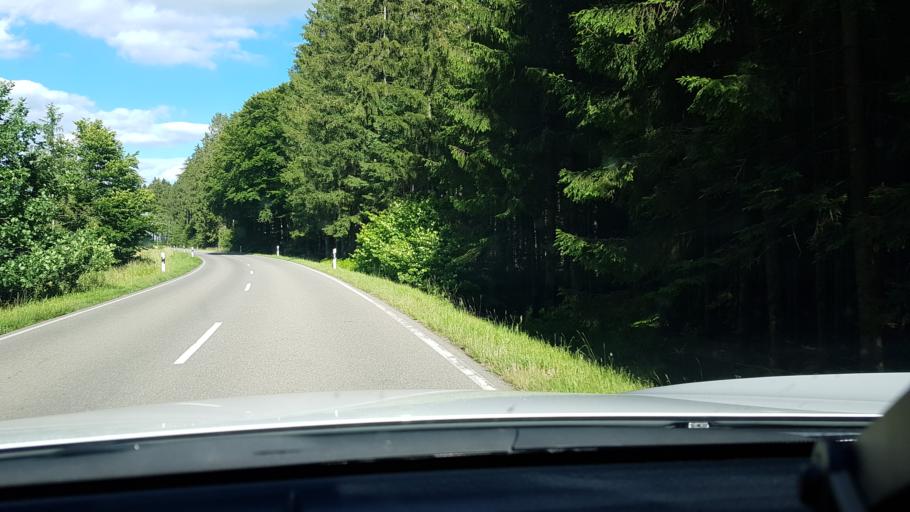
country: DE
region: Baden-Wuerttemberg
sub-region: Tuebingen Region
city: Kirchberg an der Iller
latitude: 48.1243
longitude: 10.0404
